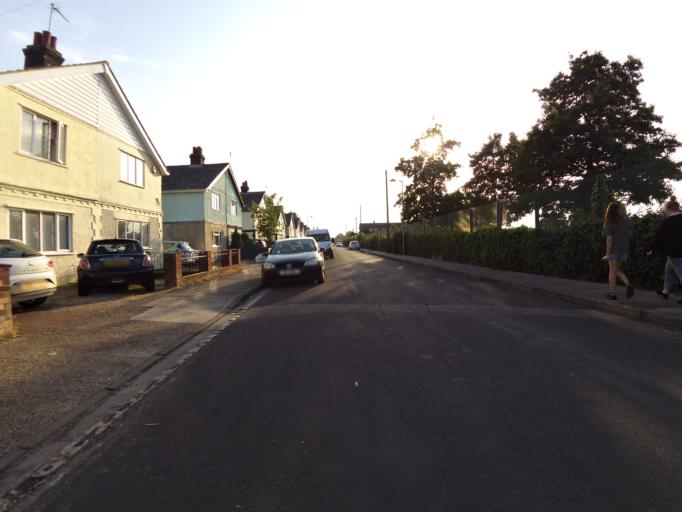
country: GB
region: England
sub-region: Suffolk
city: Ipswich
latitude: 52.0557
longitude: 1.1933
